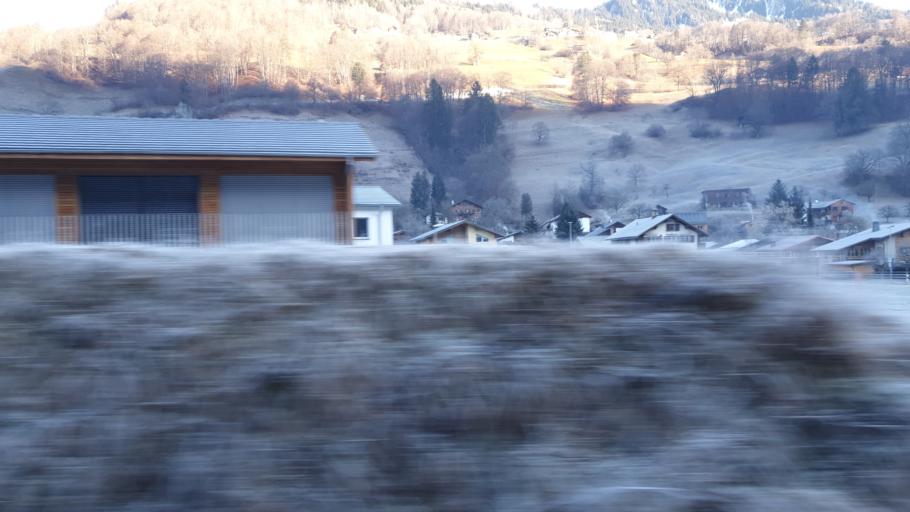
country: CH
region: Grisons
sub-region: Praettigau/Davos District
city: Grusch
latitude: 46.9787
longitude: 9.6530
